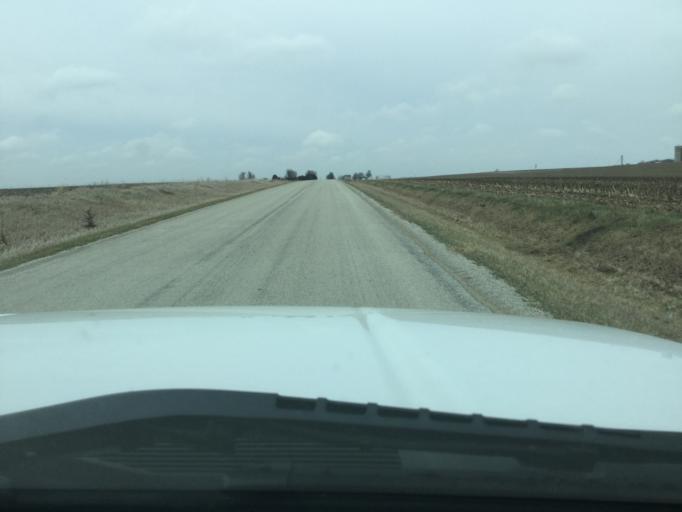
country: US
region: Kansas
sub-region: Nemaha County
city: Sabetha
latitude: 39.8503
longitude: -95.7142
